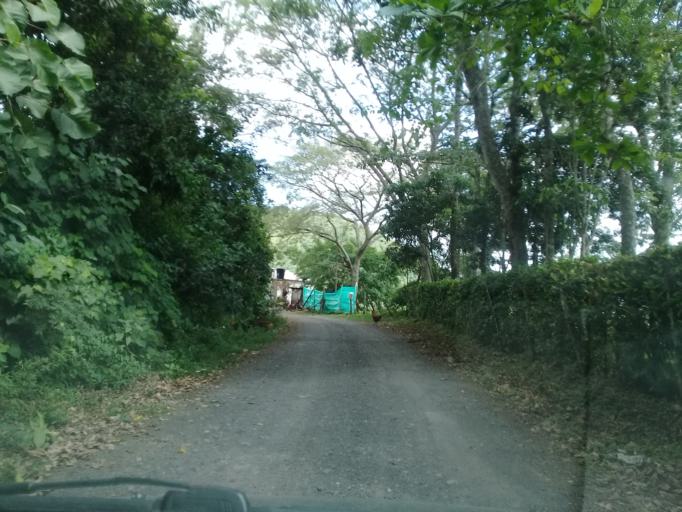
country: CO
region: Cundinamarca
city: Viani
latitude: 4.8699
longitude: -74.5390
